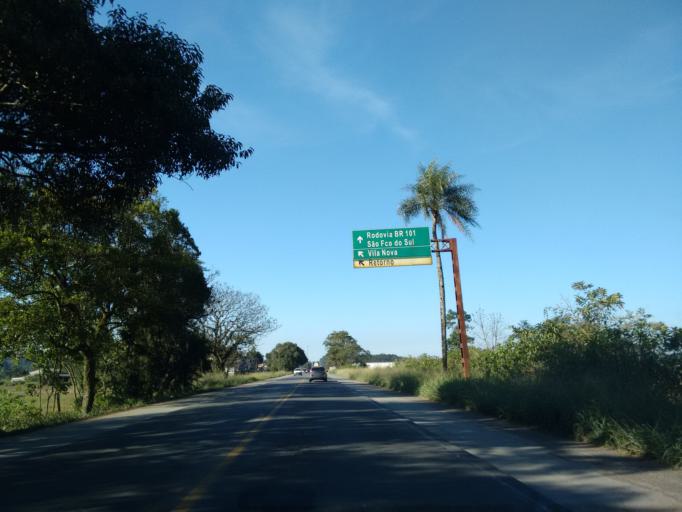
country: BR
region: Santa Catarina
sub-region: Guaramirim
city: Guaramirim
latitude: -26.4693
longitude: -48.9659
